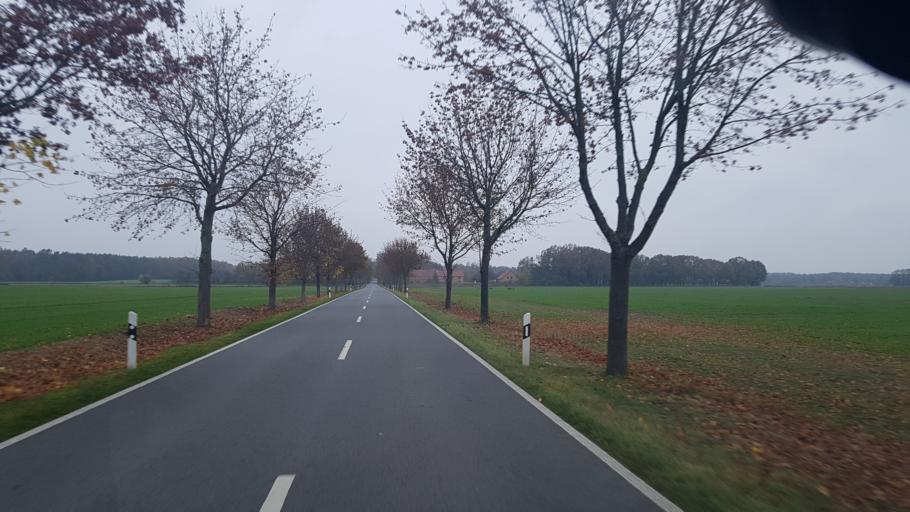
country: DE
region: Brandenburg
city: Lindow
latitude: 52.9472
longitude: 13.0112
